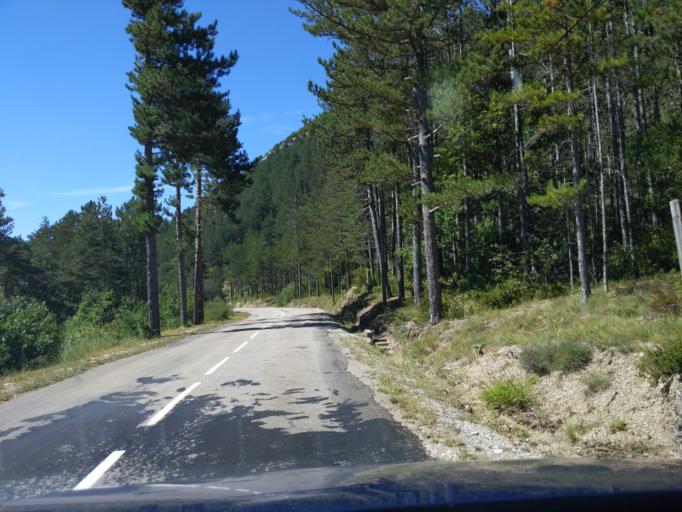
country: FR
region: Rhone-Alpes
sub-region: Departement de la Drome
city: Die
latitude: 44.6100
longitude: 5.4779
